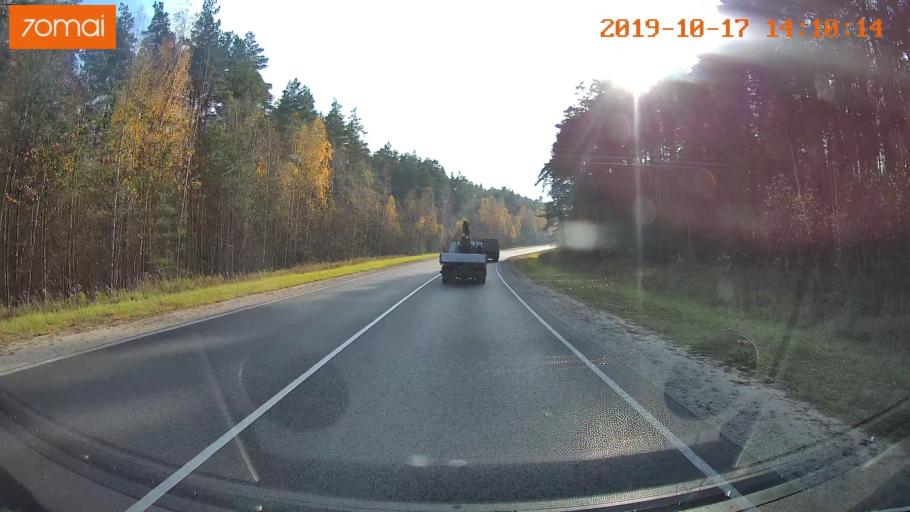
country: RU
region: Rjazan
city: Spas-Klepiki
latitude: 55.0810
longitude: 40.0521
